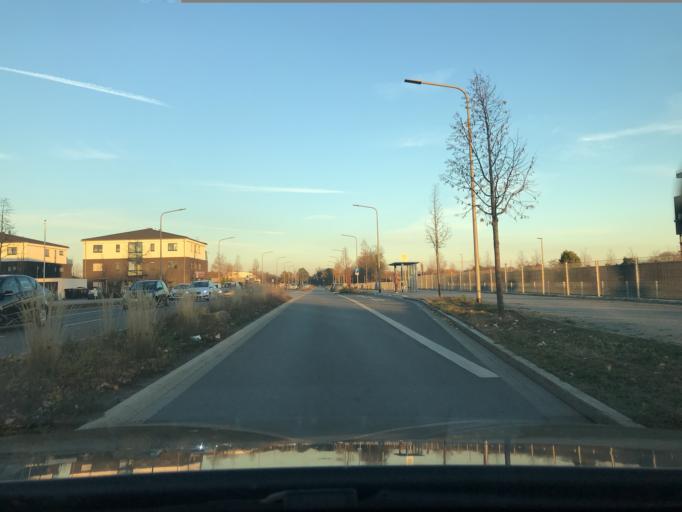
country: DE
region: North Rhine-Westphalia
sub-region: Regierungsbezirk Dusseldorf
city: Kamp-Lintfort
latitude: 51.4411
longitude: 6.5533
